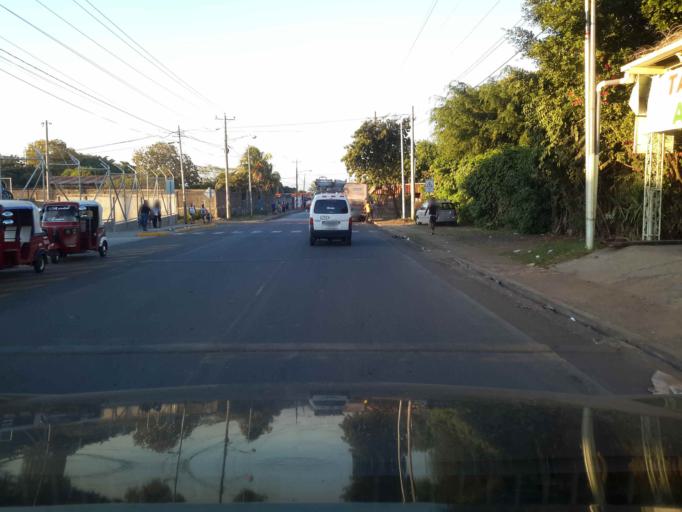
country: NI
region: Managua
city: Managua
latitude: 12.1038
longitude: -86.2332
